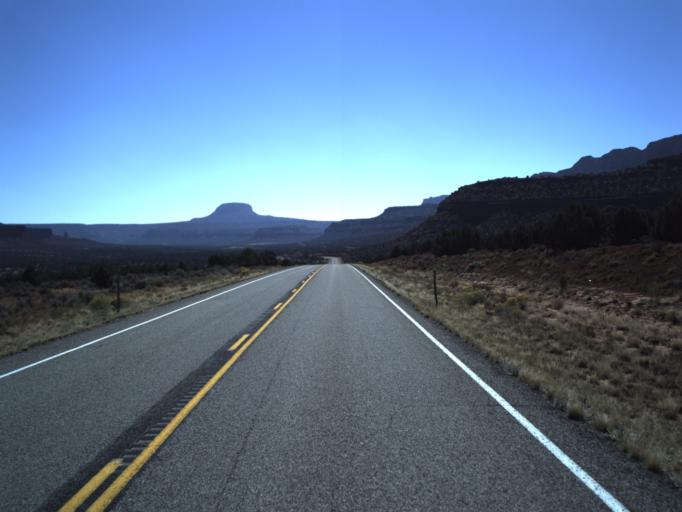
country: US
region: Utah
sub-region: San Juan County
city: Blanding
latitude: 37.6493
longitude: -110.1694
